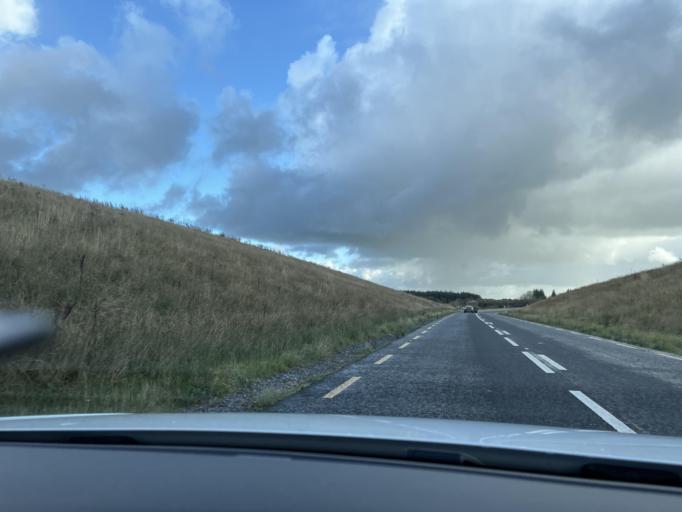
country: IE
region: Connaught
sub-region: Roscommon
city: Boyle
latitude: 53.8989
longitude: -8.2542
